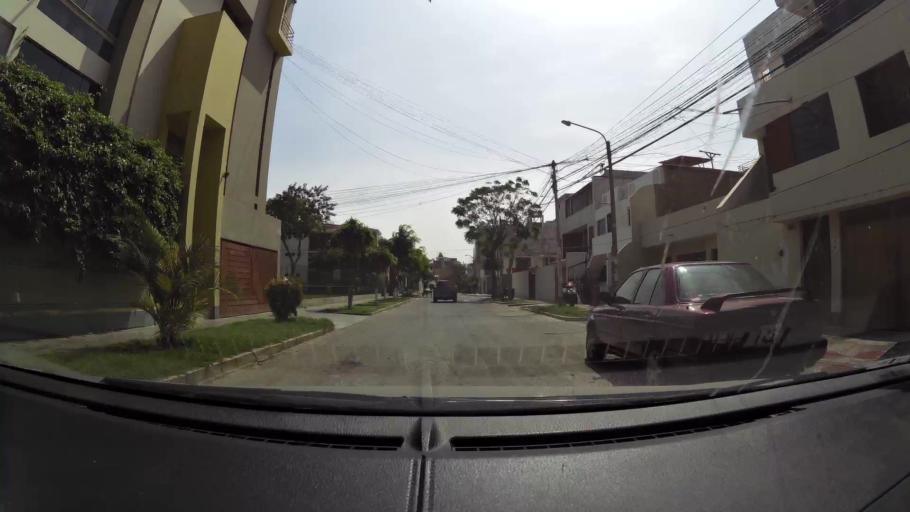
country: PE
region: La Libertad
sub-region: Provincia de Trujillo
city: Buenos Aires
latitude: -8.1273
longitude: -79.0376
